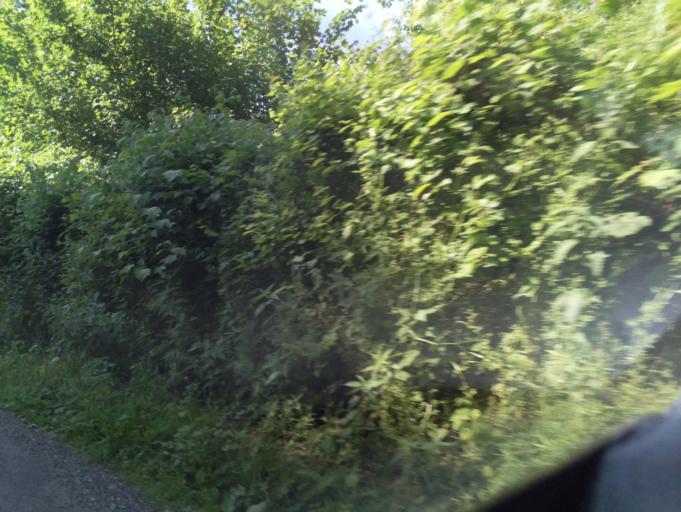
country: GB
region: England
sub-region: Hampshire
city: Overton
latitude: 51.2140
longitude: -1.3605
